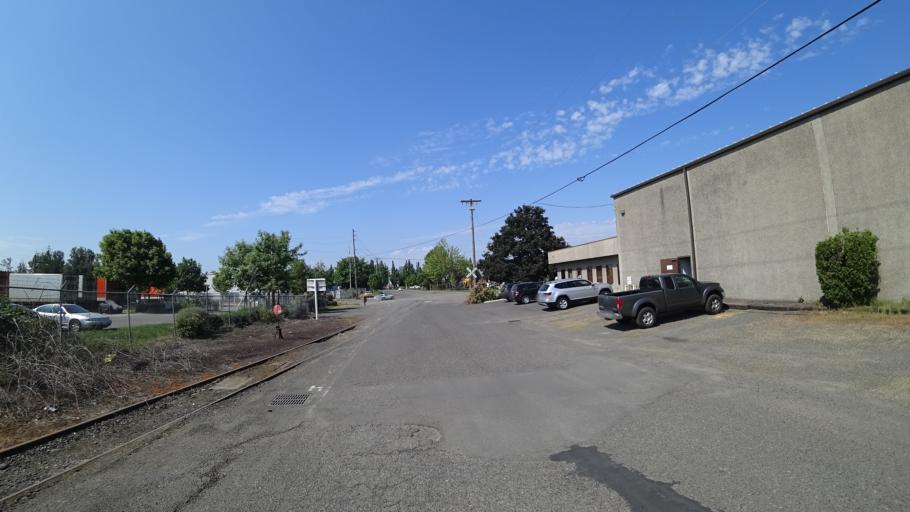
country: US
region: Oregon
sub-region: Multnomah County
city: Lents
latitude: 45.5579
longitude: -122.5289
